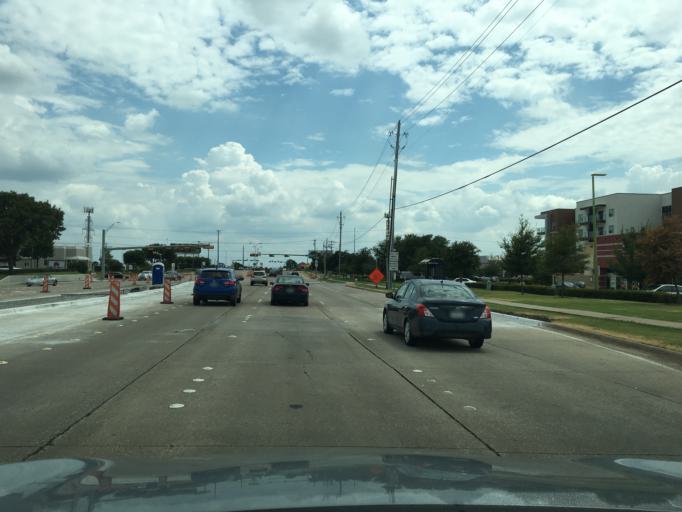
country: US
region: Texas
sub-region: Dallas County
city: Addison
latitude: 33.0159
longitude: -96.7954
